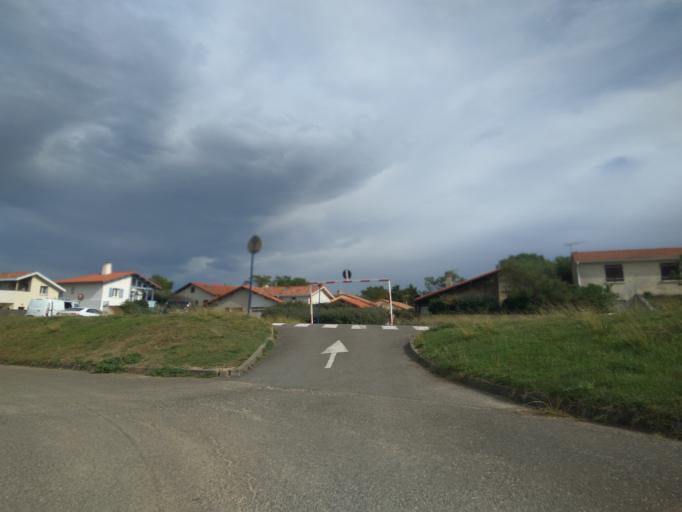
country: FR
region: Aquitaine
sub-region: Departement des Landes
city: Capbreton
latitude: 43.6463
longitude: -1.4429
